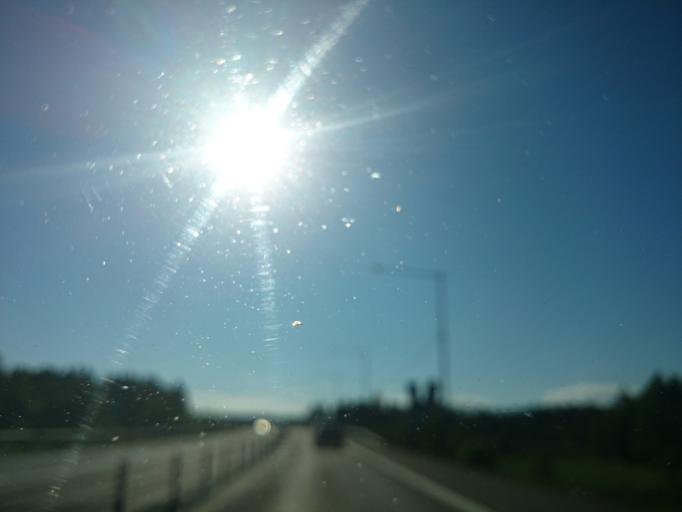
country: SE
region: Vaesternorrland
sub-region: Timra Kommun
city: Bergeforsen
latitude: 62.5181
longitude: 17.4385
